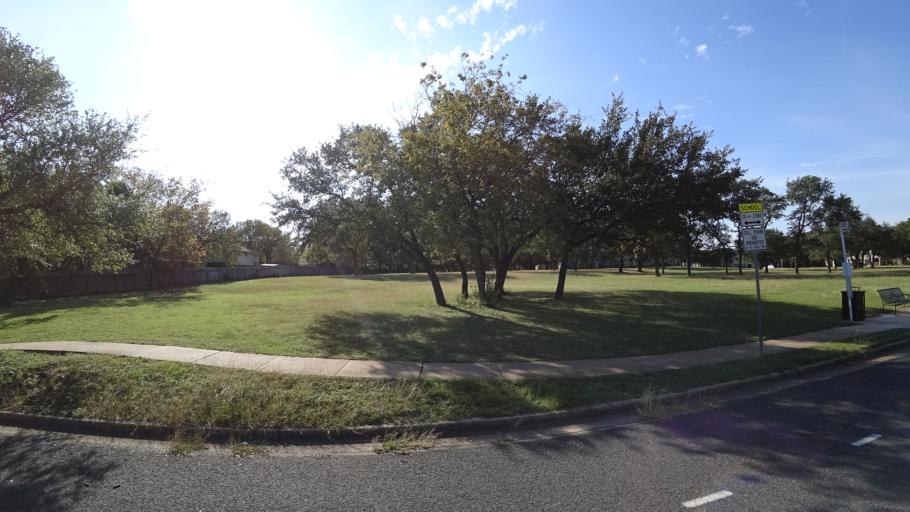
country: US
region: Texas
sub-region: Williamson County
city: Anderson Mill
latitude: 30.4532
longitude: -97.8032
